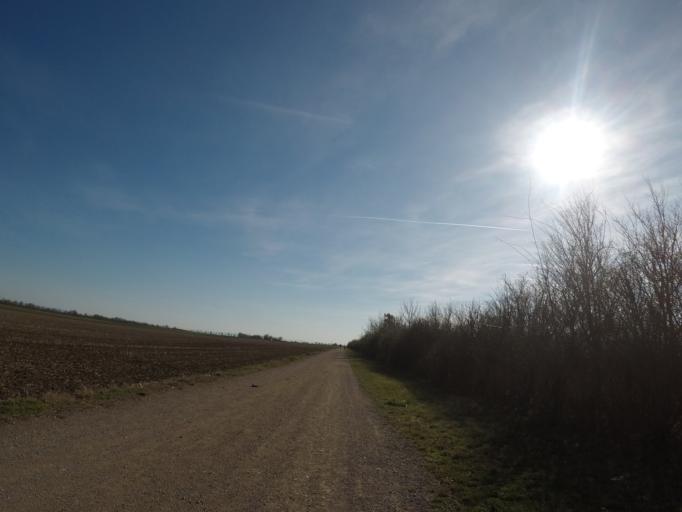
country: AT
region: Lower Austria
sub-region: Politischer Bezirk Modling
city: Vosendorf
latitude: 48.1118
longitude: 16.3402
